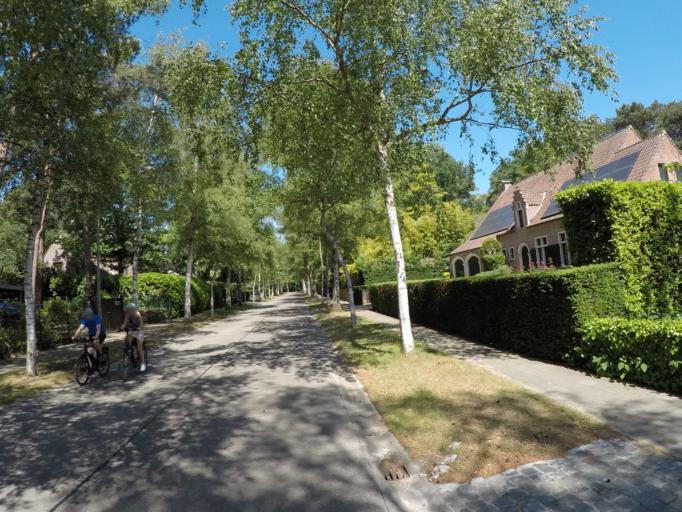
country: BE
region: Flanders
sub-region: Provincie Antwerpen
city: Kapellen
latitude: 51.2969
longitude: 4.4610
